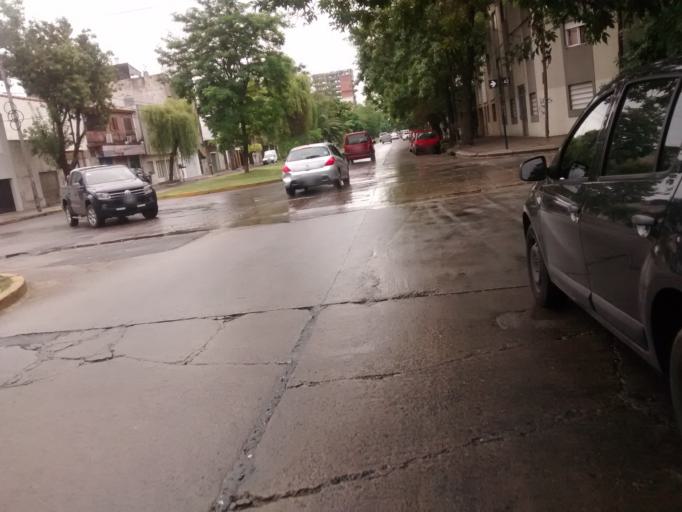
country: AR
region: Buenos Aires
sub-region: Partido de La Plata
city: La Plata
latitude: -34.9203
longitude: -57.9696
